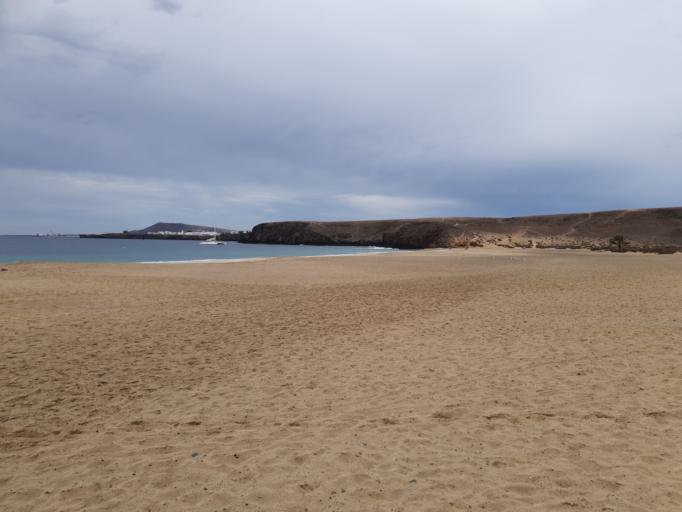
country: ES
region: Canary Islands
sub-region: Provincia de Las Palmas
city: Playa Blanca
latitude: 28.8522
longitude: -13.7919
